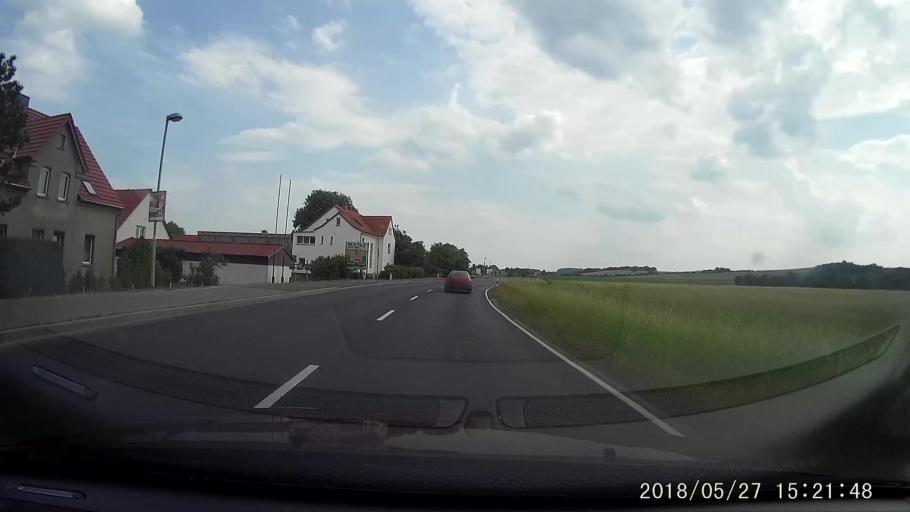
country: DE
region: Saxony
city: Kodersdorf
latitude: 51.2382
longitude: 14.8895
